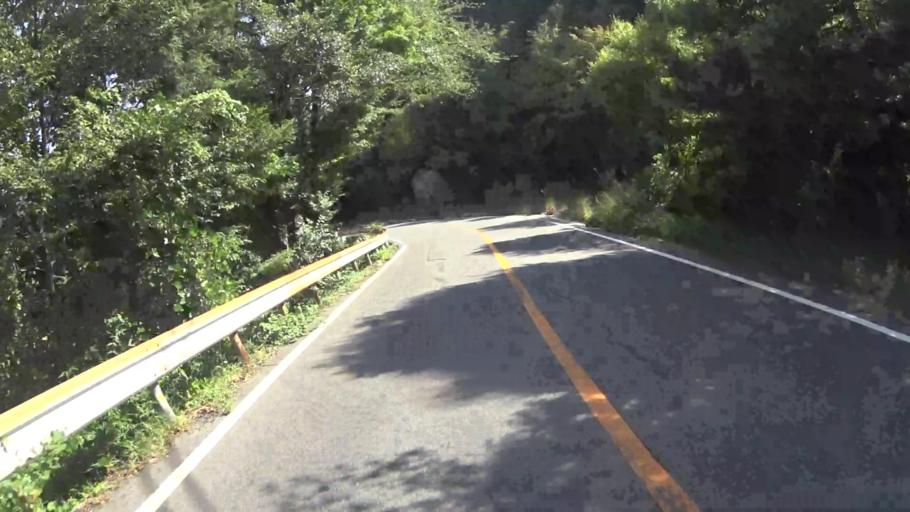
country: JP
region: Kyoto
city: Kameoka
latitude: 34.9852
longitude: 135.5345
